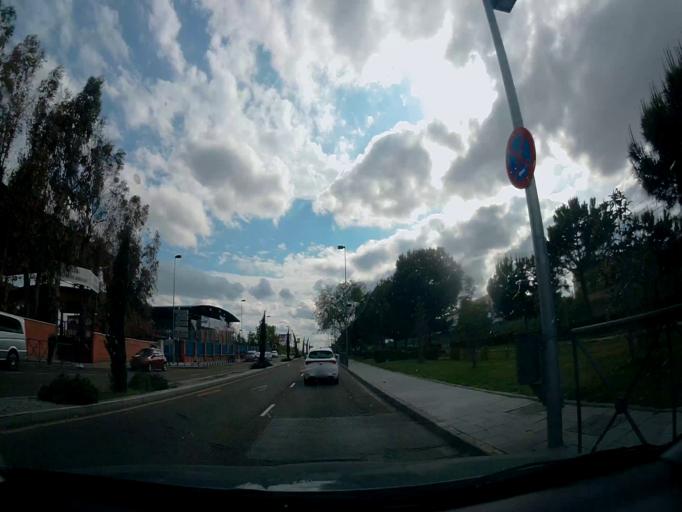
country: ES
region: Madrid
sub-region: Provincia de Madrid
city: Alcorcon
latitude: 40.3451
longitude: -3.8378
